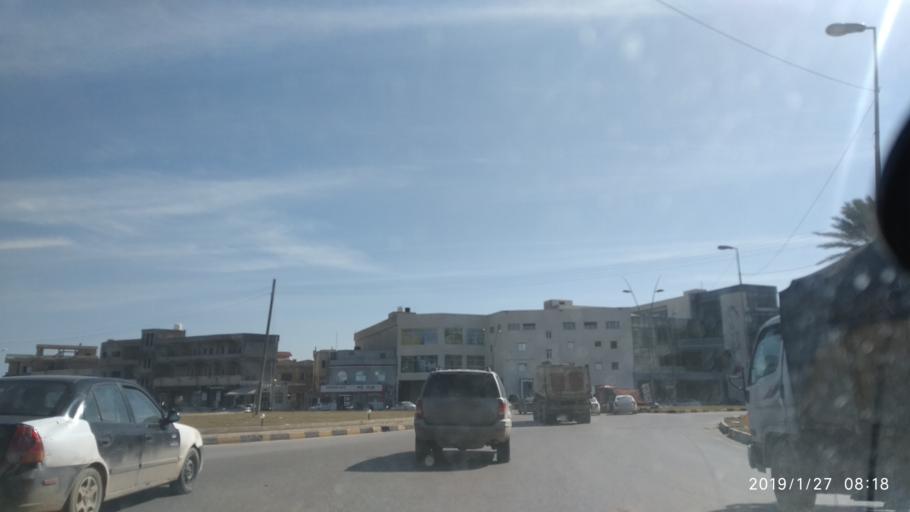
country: LY
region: Tripoli
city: Tagiura
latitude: 32.8940
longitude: 13.3428
